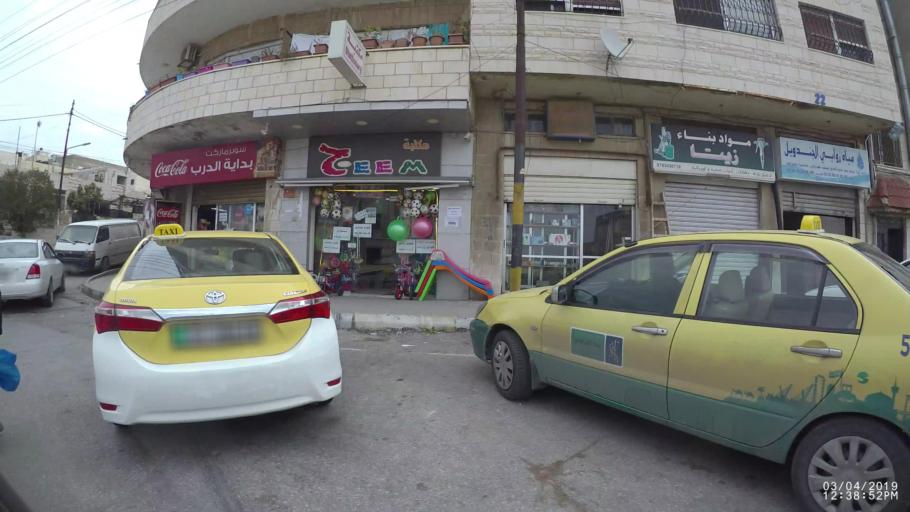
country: JO
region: Amman
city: Wadi as Sir
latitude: 31.9565
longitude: 35.8349
